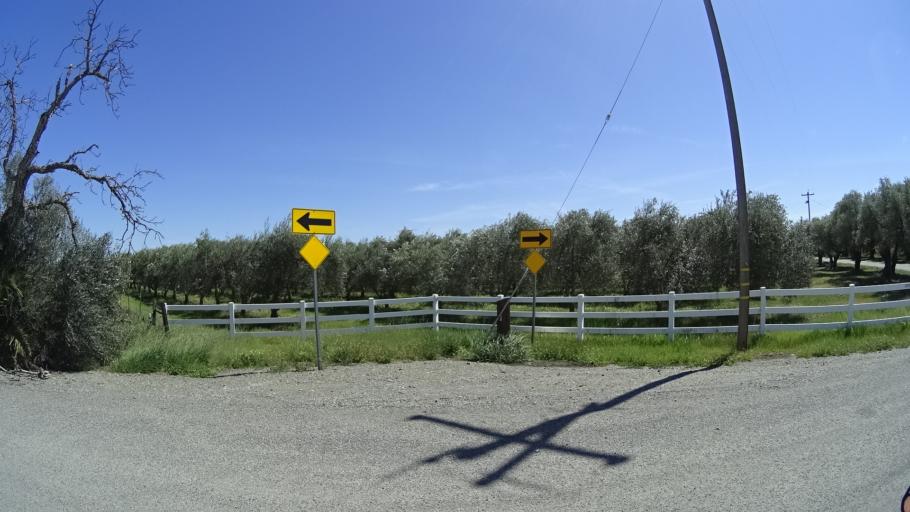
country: US
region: California
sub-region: Glenn County
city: Orland
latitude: 39.7397
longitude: -122.1503
